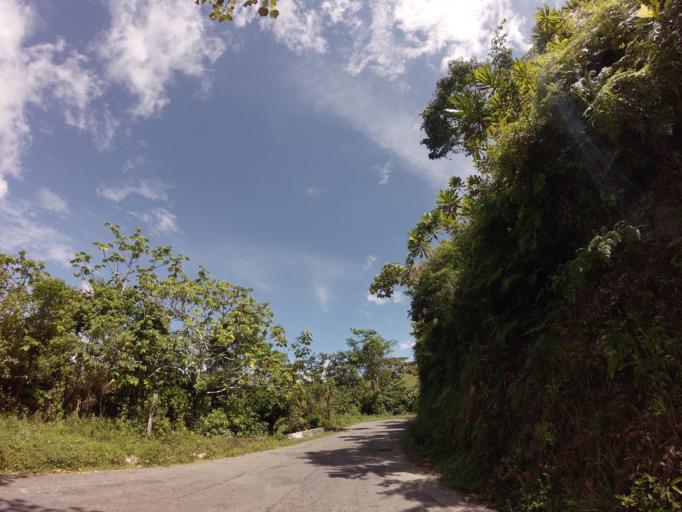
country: CO
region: Caldas
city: Norcasia
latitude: 5.5816
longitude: -74.8772
